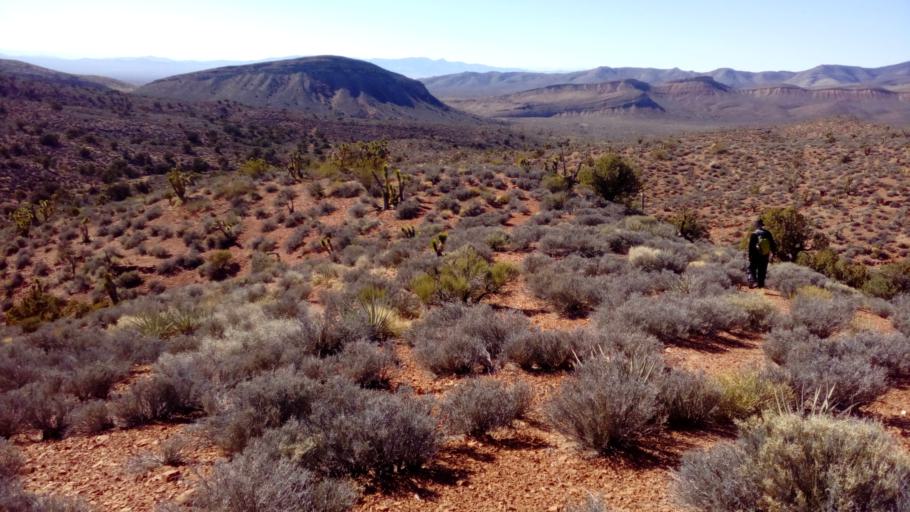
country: US
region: Nevada
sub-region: Clark County
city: Summerlin South
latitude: 36.0610
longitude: -115.5734
